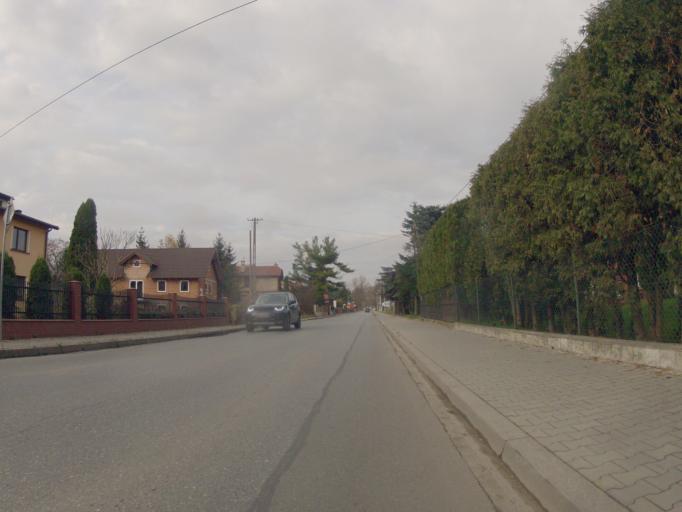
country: PL
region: Lesser Poland Voivodeship
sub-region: Powiat krakowski
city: Rzaska
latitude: 50.0853
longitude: 19.8440
